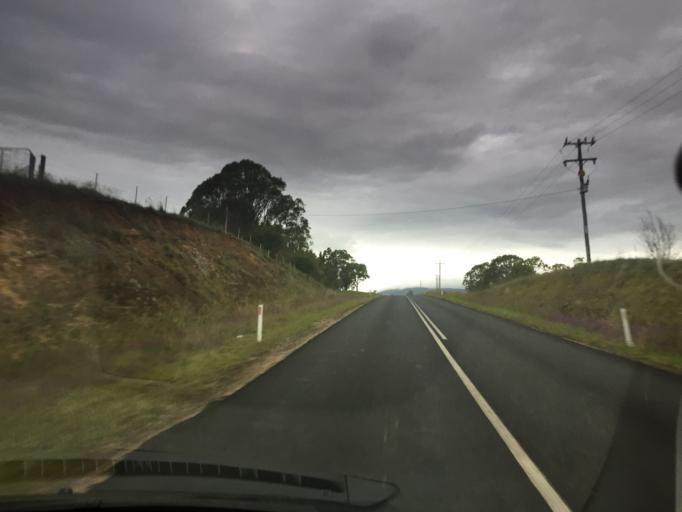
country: AU
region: New South Wales
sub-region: Bega Valley
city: Bega
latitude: -36.6494
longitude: 149.5836
